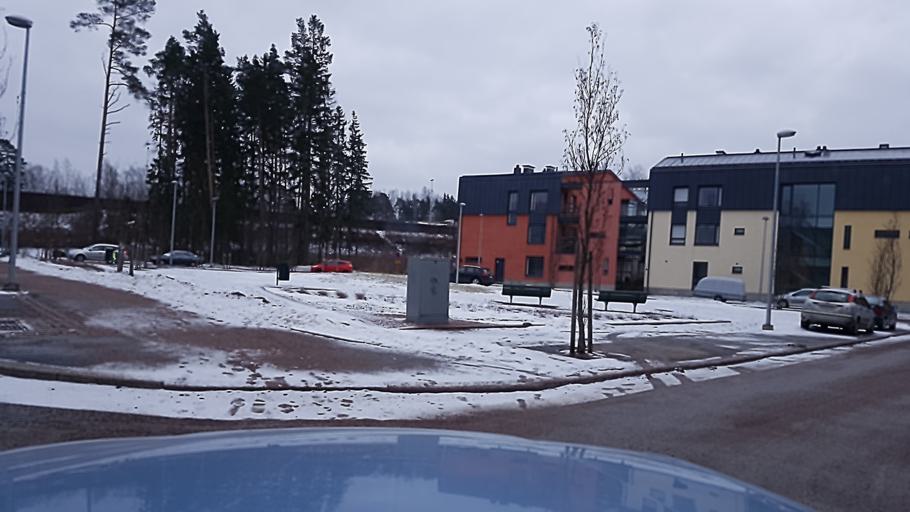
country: FI
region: Uusimaa
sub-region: Helsinki
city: Vantaa
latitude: 60.2620
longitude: 25.0696
